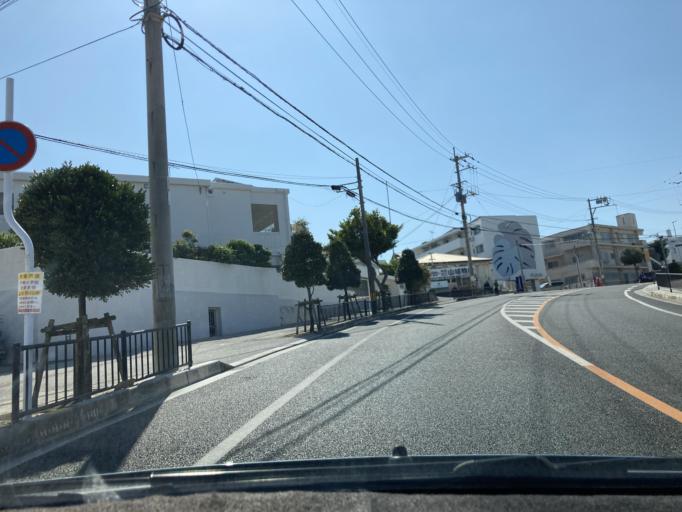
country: JP
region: Okinawa
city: Naha-shi
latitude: 26.2305
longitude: 127.7200
